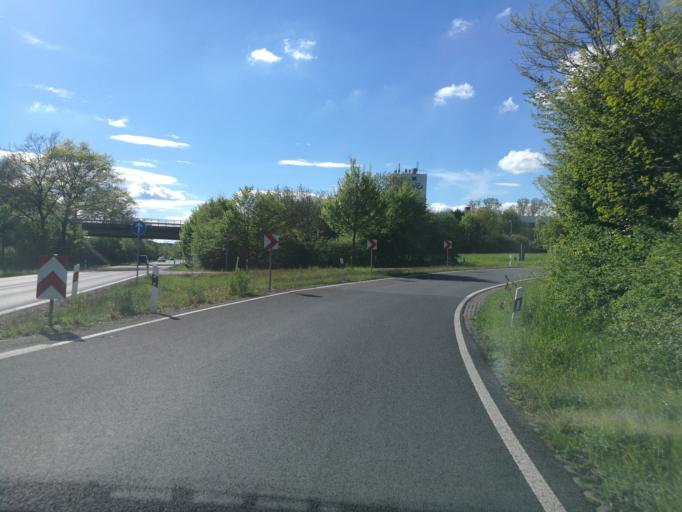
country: DE
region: Bavaria
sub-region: Upper Franconia
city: Sonnefeld
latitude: 50.2143
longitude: 11.0778
